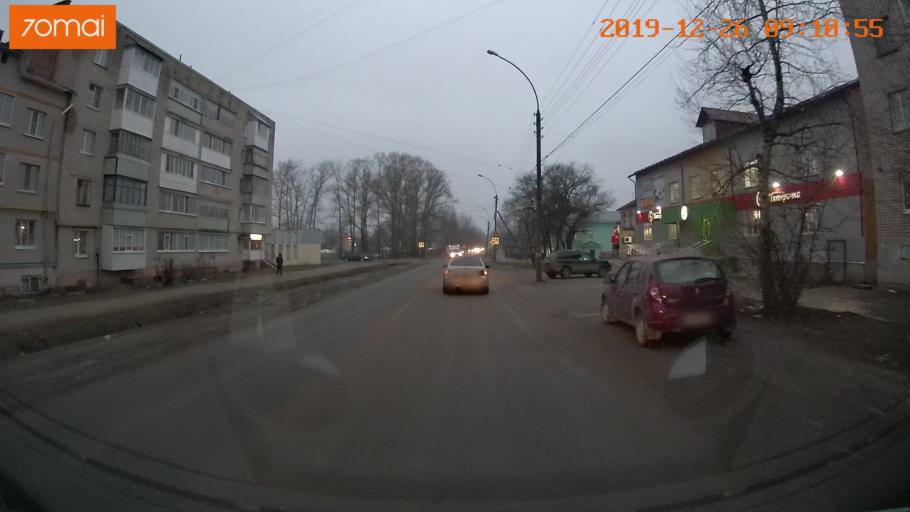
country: RU
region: Vologda
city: Gryazovets
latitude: 58.8735
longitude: 40.2525
